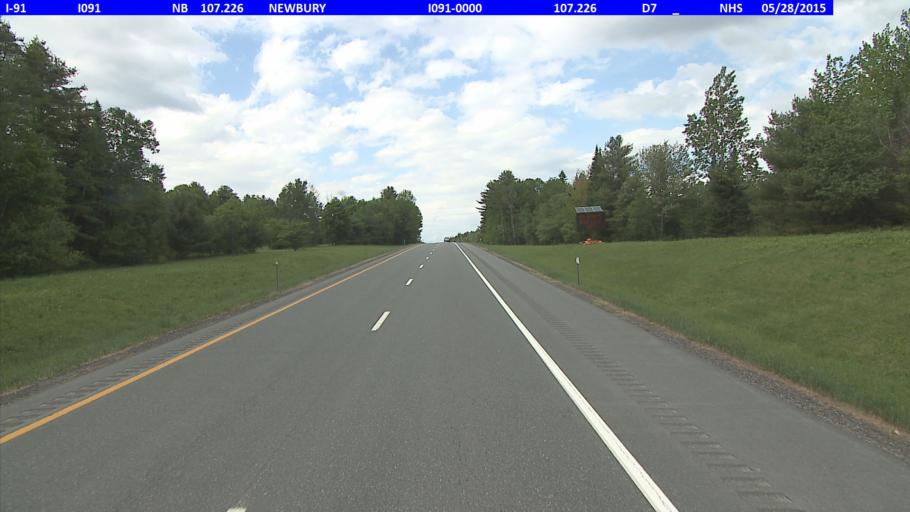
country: US
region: New Hampshire
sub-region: Grafton County
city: Woodsville
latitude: 44.1171
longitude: -72.1055
